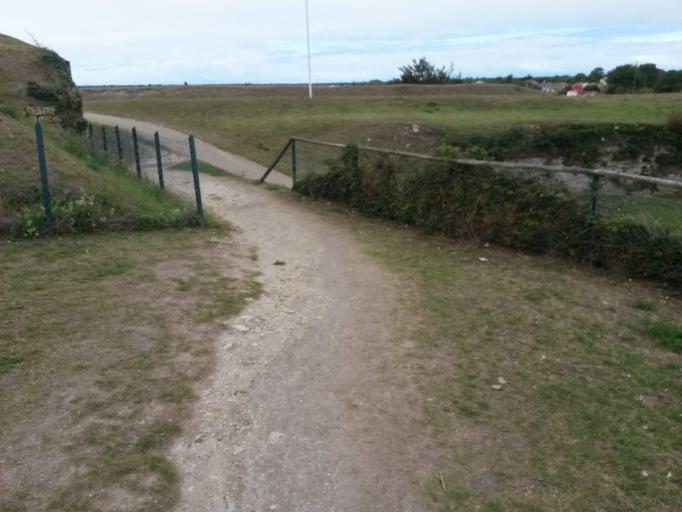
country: FR
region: Poitou-Charentes
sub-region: Departement de la Charente-Maritime
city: Saint-Trojan-les-Bains
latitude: 45.8838
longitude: -1.1888
